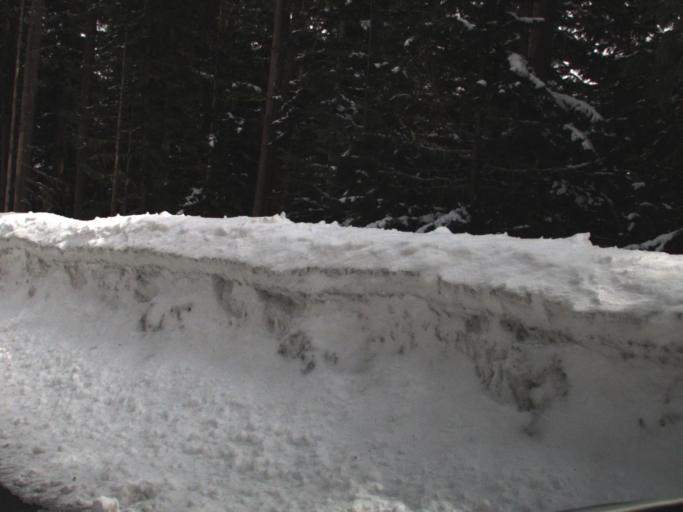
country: US
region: Washington
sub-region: Kittitas County
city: Cle Elum
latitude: 46.9118
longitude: -121.4102
